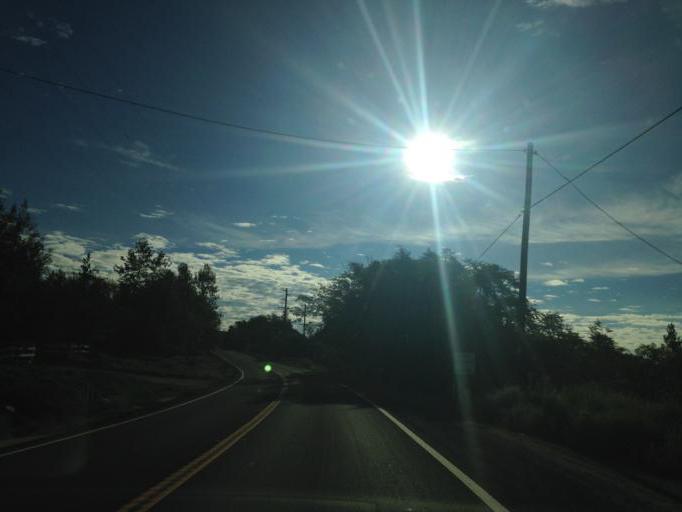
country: US
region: California
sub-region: San Diego County
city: Valley Center
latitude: 33.2946
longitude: -116.9044
